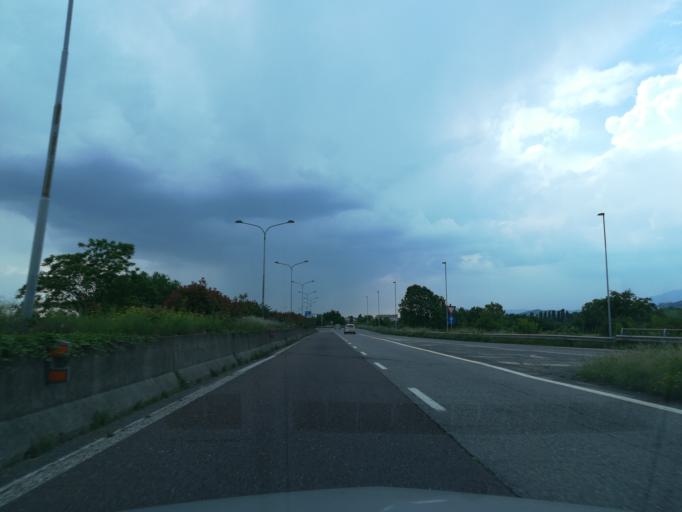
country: IT
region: Lombardy
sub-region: Provincia di Bergamo
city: Orio al Serio
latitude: 45.6797
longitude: 9.6959
